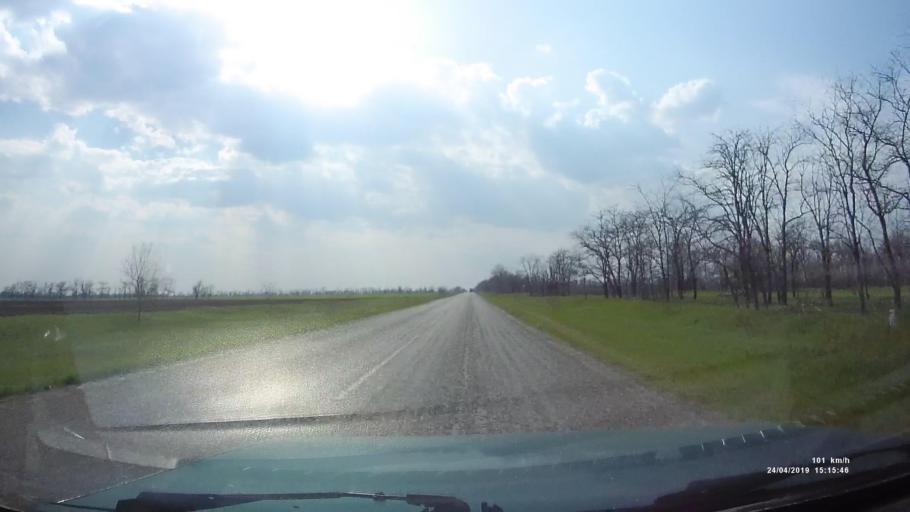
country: RU
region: Rostov
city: Remontnoye
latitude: 46.5465
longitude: 43.2277
